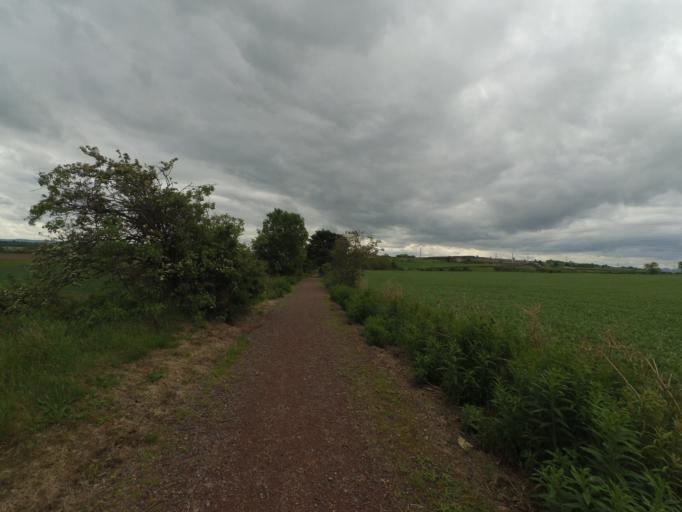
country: GB
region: Scotland
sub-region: East Lothian
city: Ormiston
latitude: 55.9153
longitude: -2.9657
